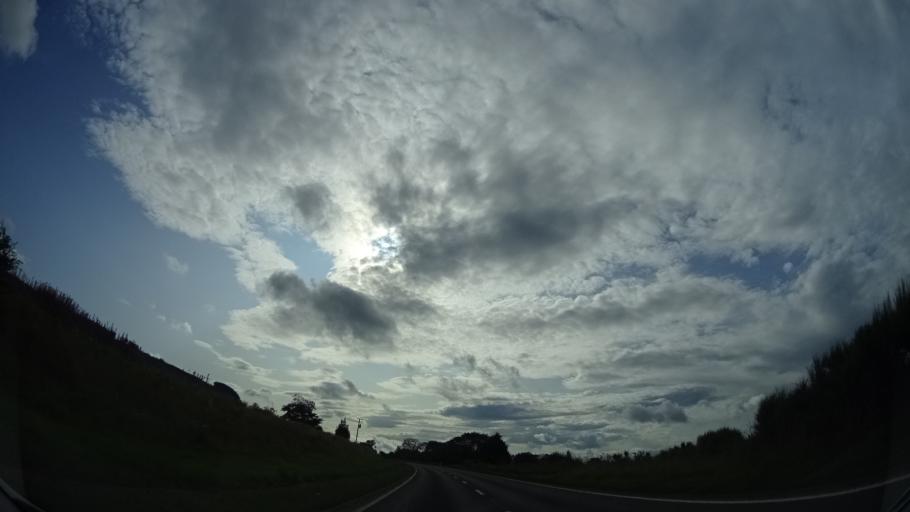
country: GB
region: Scotland
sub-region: Highland
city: Muir of Ord
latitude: 57.5587
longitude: -4.5465
